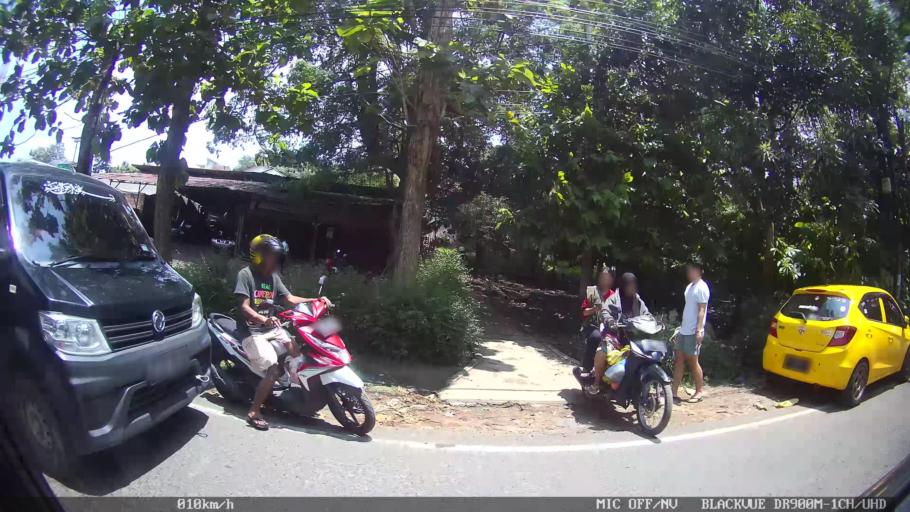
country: ID
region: Lampung
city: Kedaton
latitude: -5.4009
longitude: 105.2551
